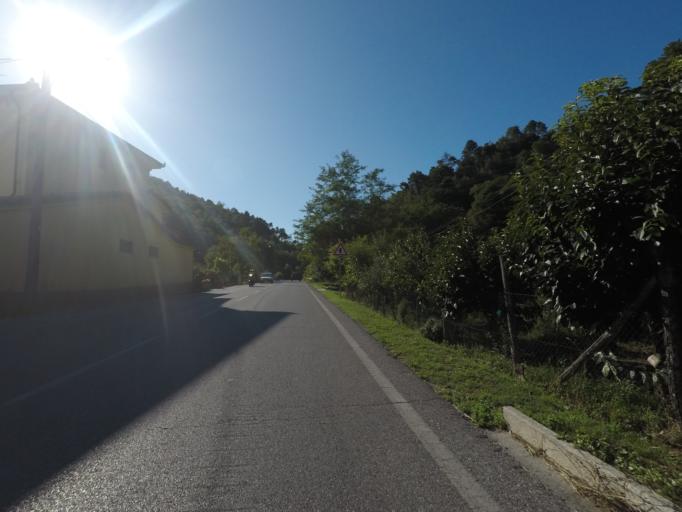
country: IT
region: Tuscany
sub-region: Provincia di Lucca
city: Massarosa
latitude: 43.9017
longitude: 10.3785
